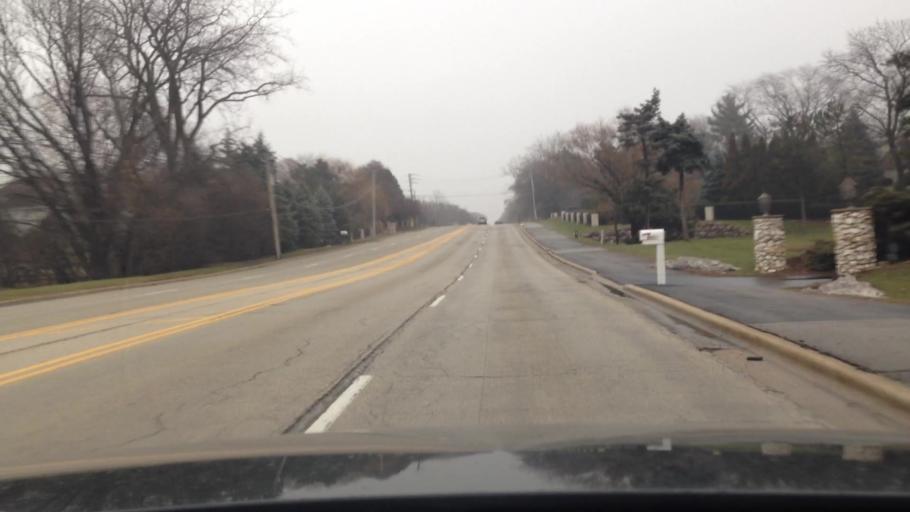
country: US
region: Illinois
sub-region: DuPage County
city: Oakbrook Terrace
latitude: 41.8314
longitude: -87.9888
